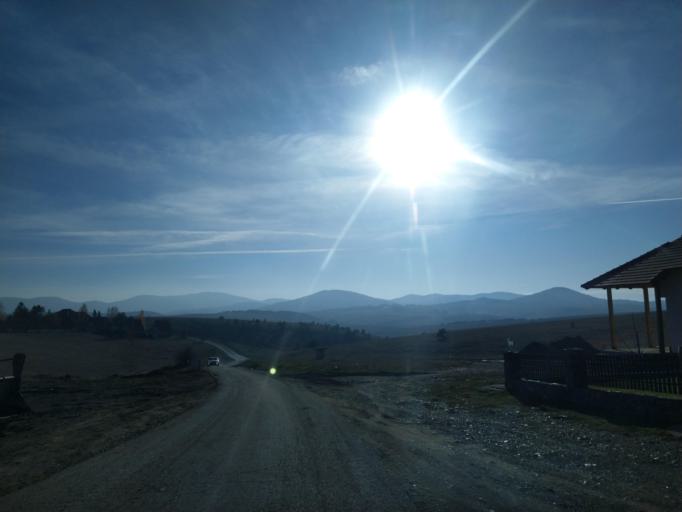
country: RS
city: Zlatibor
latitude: 43.7415
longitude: 19.6764
